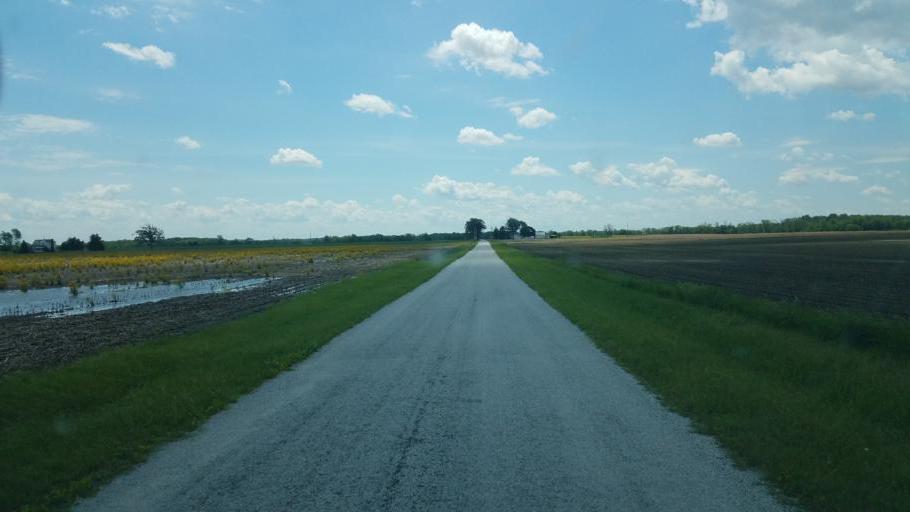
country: US
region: Ohio
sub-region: Hardin County
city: Forest
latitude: 40.6762
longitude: -83.4598
